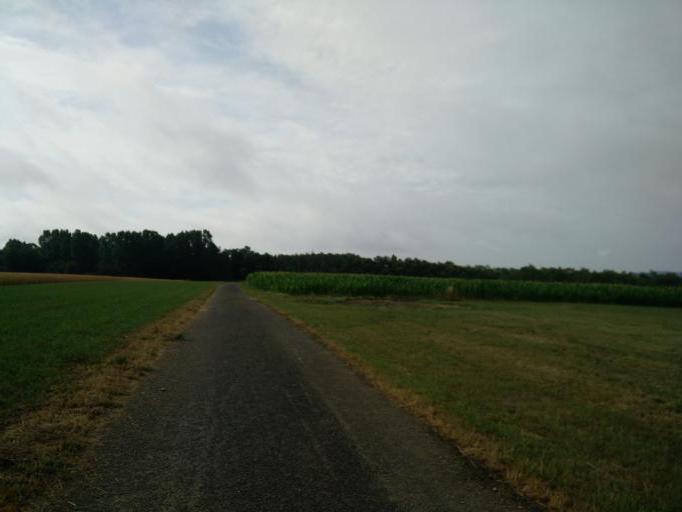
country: LU
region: Luxembourg
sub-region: Canton de Capellen
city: Mamer
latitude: 49.6336
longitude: 6.0412
